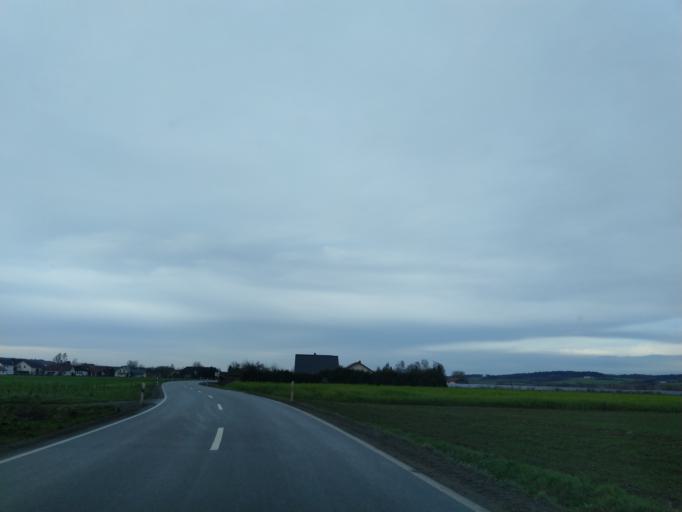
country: DE
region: Bavaria
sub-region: Lower Bavaria
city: Rossbach
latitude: 48.6239
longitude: 12.9681
